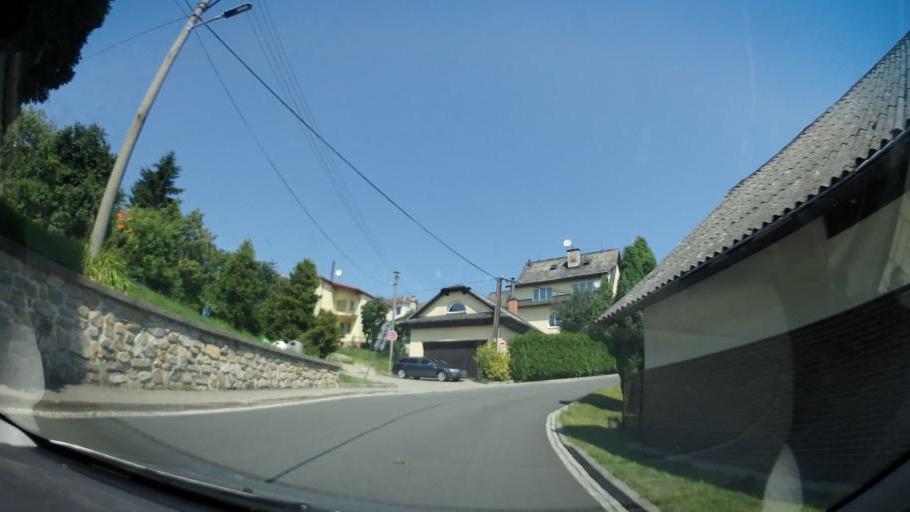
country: CZ
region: Olomoucky
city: Zabreh
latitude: 49.8751
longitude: 16.8465
